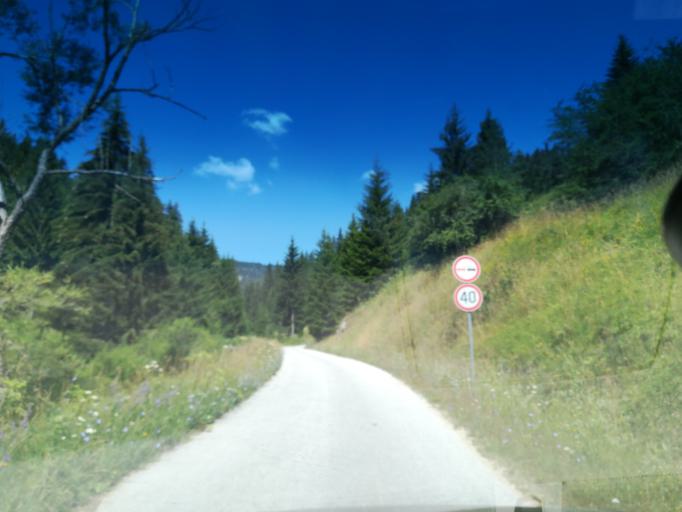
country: BG
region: Smolyan
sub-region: Obshtina Chepelare
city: Chepelare
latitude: 41.6738
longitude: 24.7903
